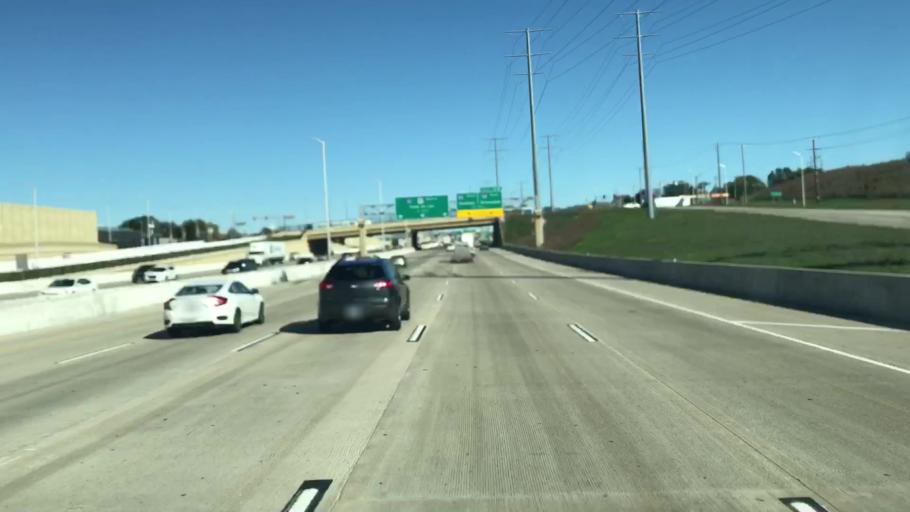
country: US
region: Wisconsin
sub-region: Milwaukee County
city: West Allis
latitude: 43.0139
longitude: -88.0362
